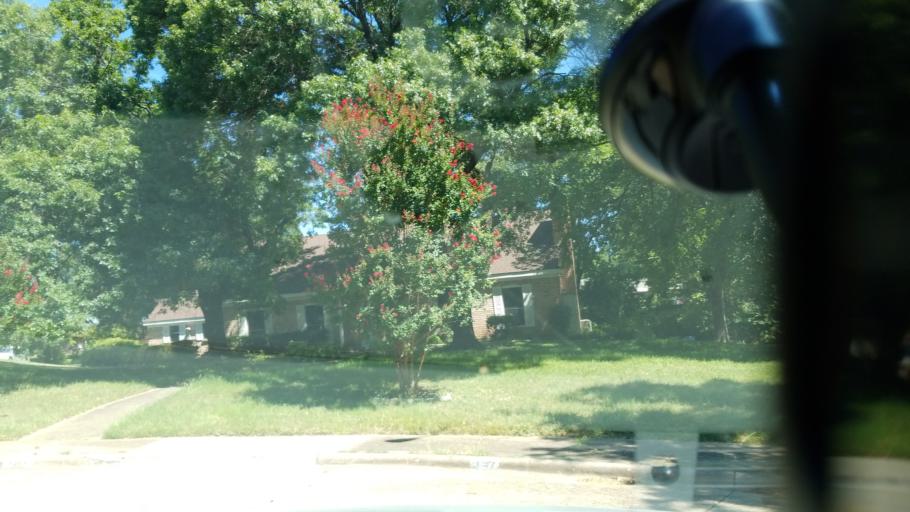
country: US
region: Texas
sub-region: Dallas County
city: Cockrell Hill
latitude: 32.6819
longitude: -96.8313
